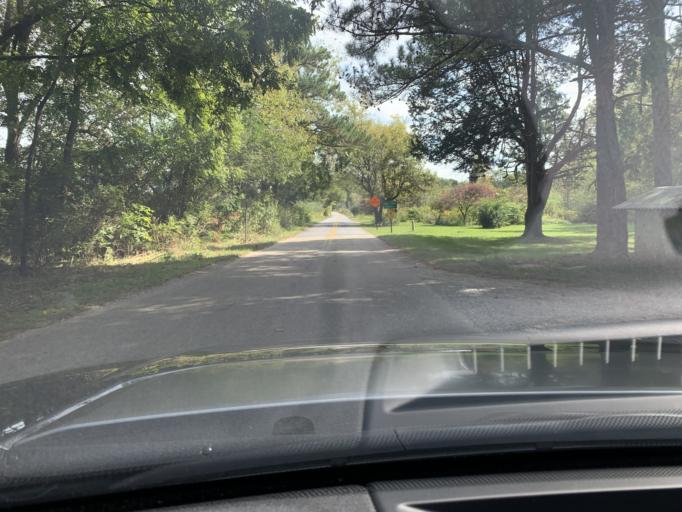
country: US
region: Georgia
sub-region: Floyd County
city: Cave Spring
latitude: 33.9492
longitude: -85.3964
